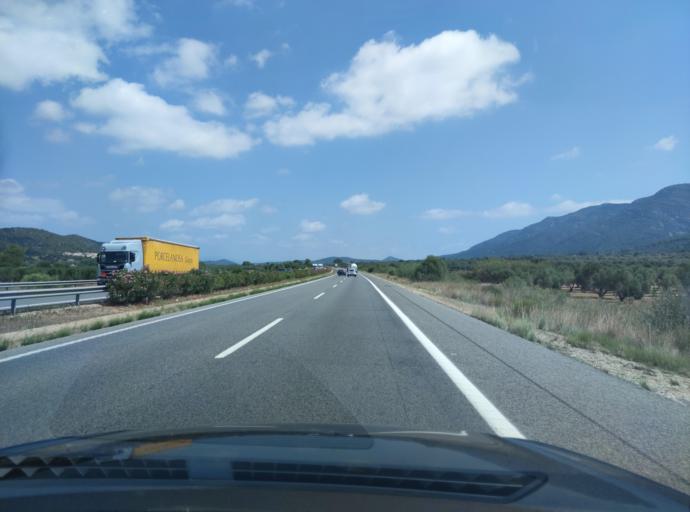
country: ES
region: Catalonia
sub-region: Provincia de Tarragona
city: Ulldecona
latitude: 40.6305
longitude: 0.4943
